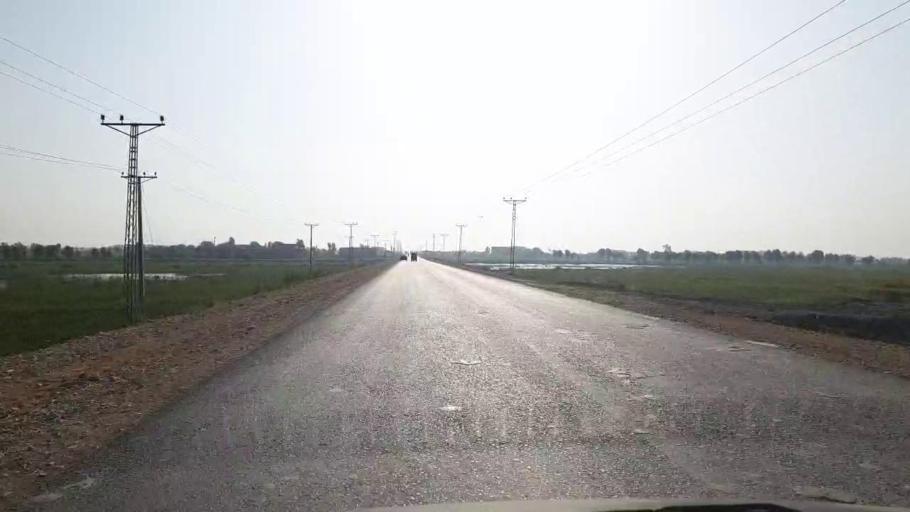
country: PK
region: Sindh
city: Badin
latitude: 24.6699
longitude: 68.8610
